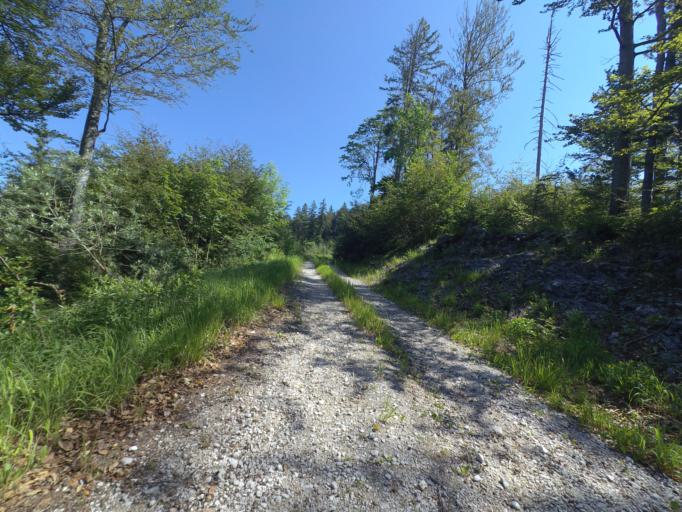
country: AT
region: Salzburg
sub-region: Politischer Bezirk Salzburg-Umgebung
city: Elsbethen
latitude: 47.7455
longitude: 13.1206
